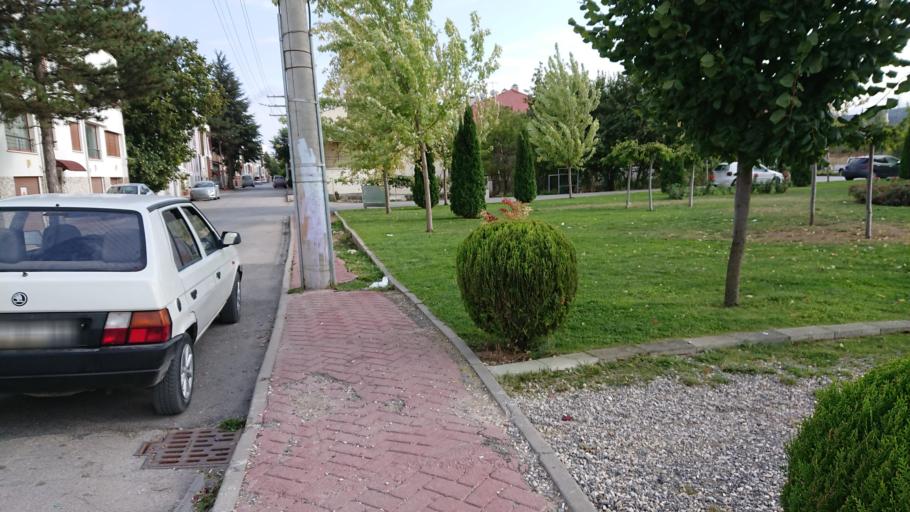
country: TR
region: Eskisehir
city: Eskisehir
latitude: 39.7624
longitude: 30.4872
